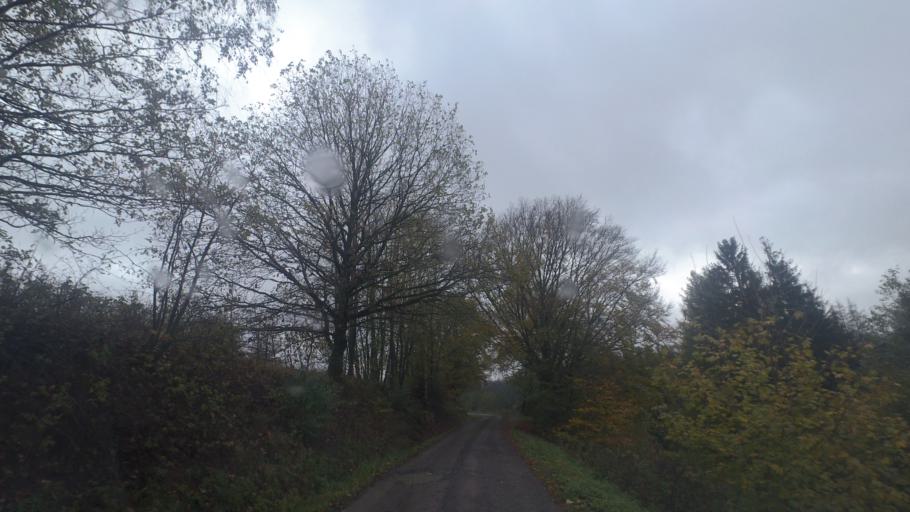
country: DE
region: Thuringia
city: Eisfeld
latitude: 50.4846
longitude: 10.8551
